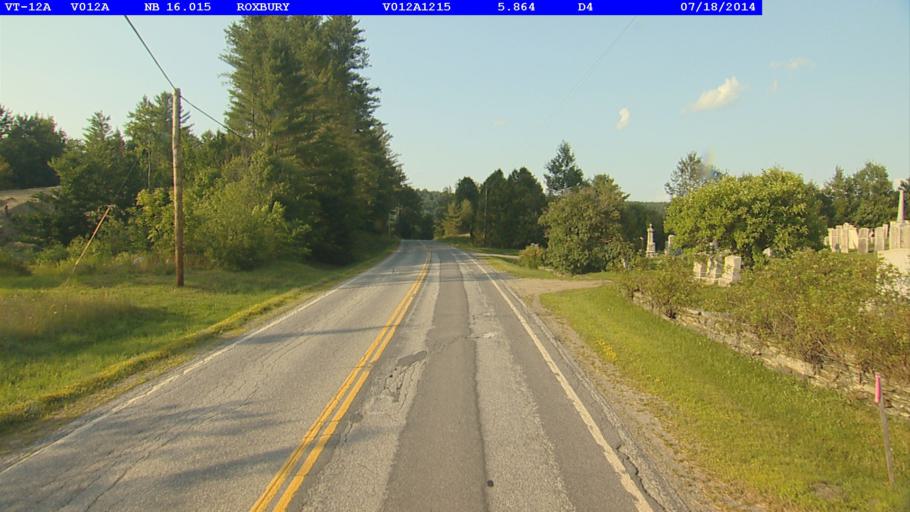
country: US
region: Vermont
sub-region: Washington County
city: Northfield
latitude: 44.1093
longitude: -72.7272
